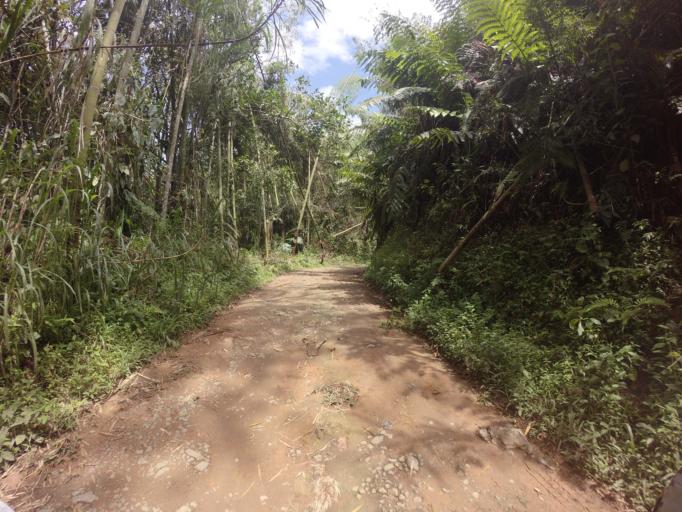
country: CO
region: Valle del Cauca
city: Ulloa
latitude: 4.7051
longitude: -75.7180
